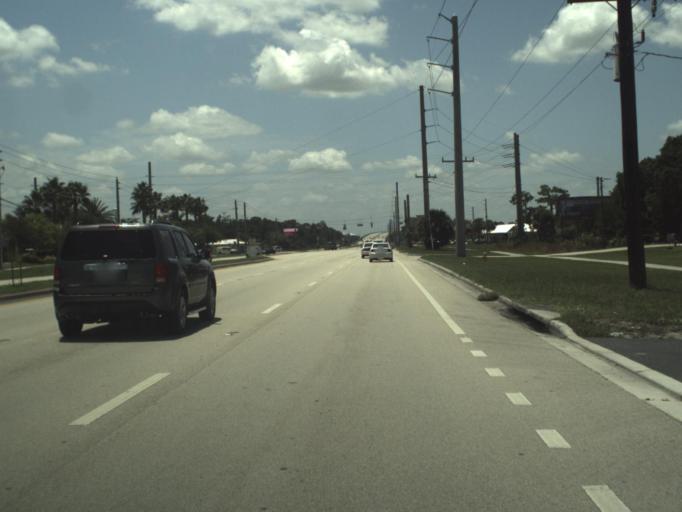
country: US
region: Florida
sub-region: Martin County
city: North River Shores
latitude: 27.2244
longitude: -80.2645
